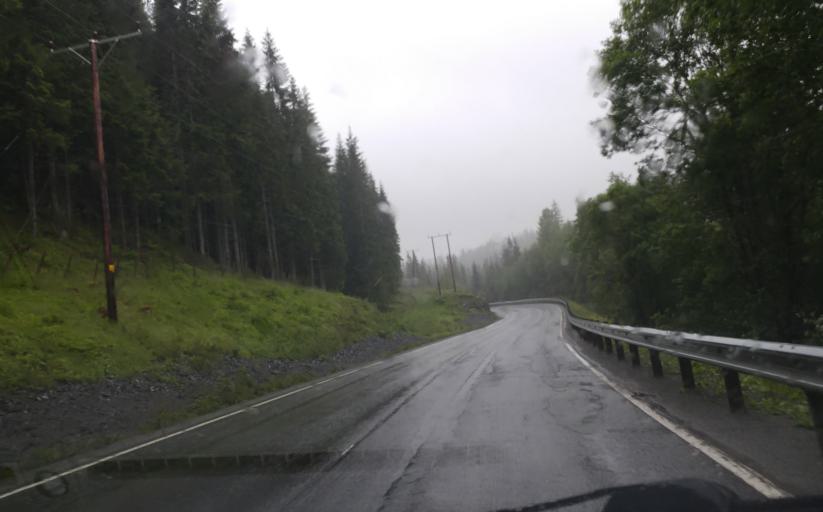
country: NO
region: Sor-Trondelag
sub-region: Selbu
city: Mebonden
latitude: 63.3473
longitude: 11.0781
